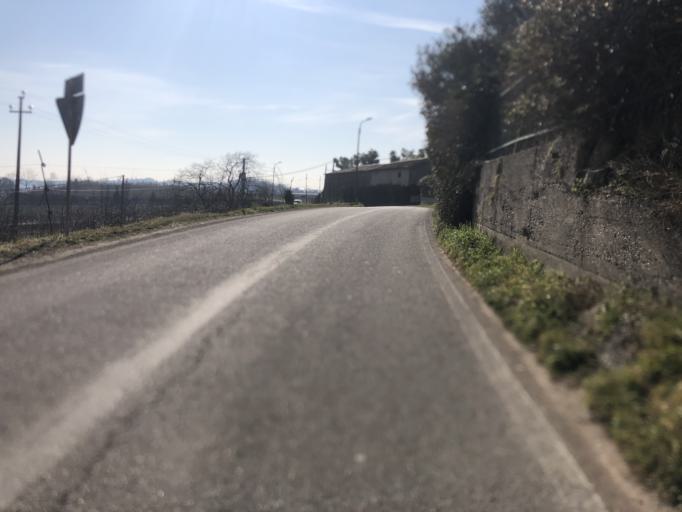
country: IT
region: Veneto
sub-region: Provincia di Verona
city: San Giorgio in Salici
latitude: 45.4062
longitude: 10.7781
